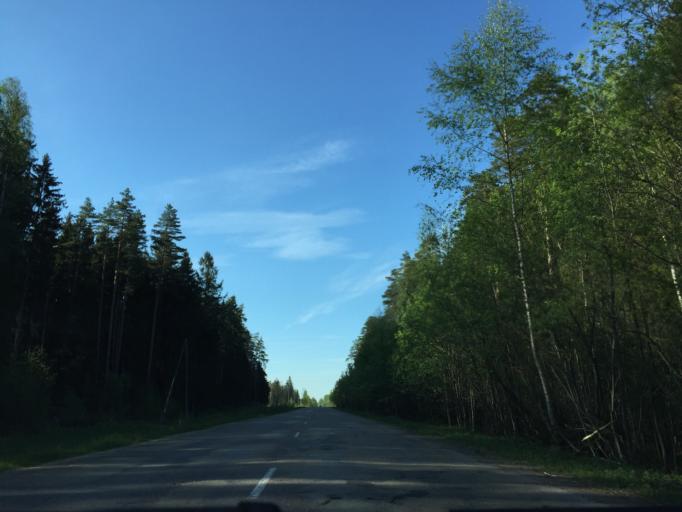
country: LV
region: Kekava
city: Balozi
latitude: 56.7227
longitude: 24.1109
